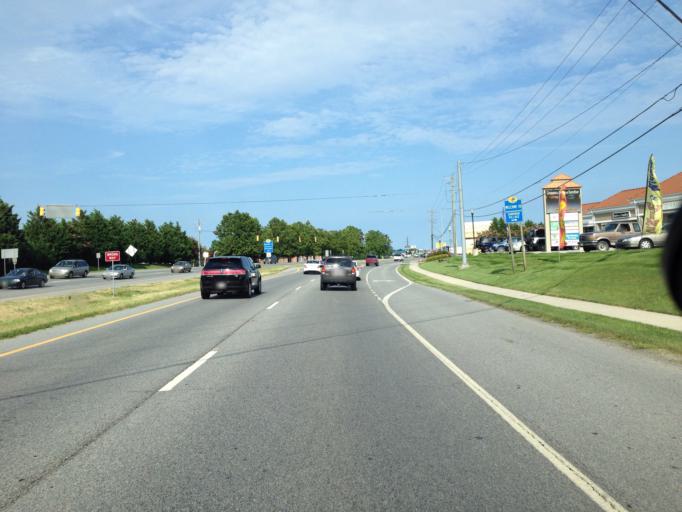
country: US
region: Delaware
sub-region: Sussex County
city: Lewes
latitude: 38.7495
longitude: -75.1837
